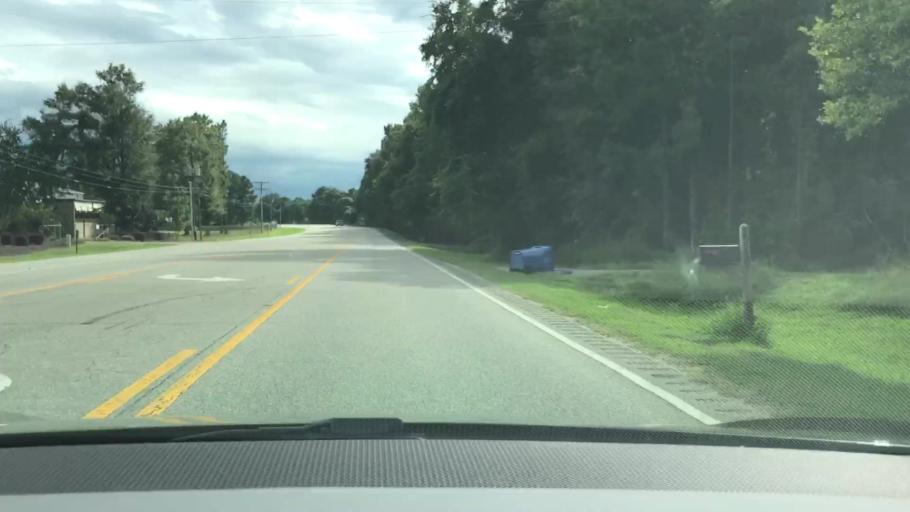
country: US
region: Alabama
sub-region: Coffee County
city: Elba
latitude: 31.5674
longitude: -86.0106
